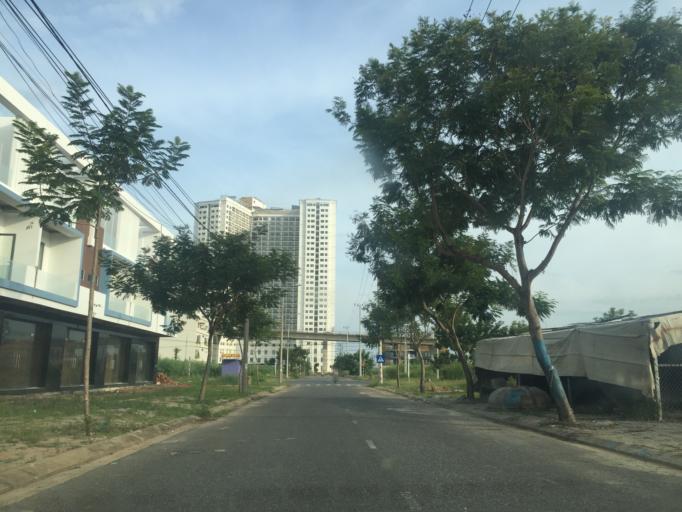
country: VN
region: Da Nang
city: Da Nang
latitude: 16.0953
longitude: 108.2264
